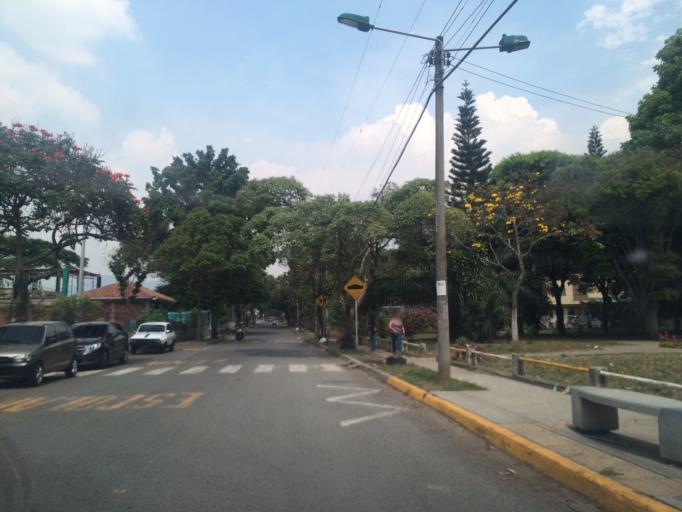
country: CO
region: Valle del Cauca
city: Cali
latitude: 3.4941
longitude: -76.4866
